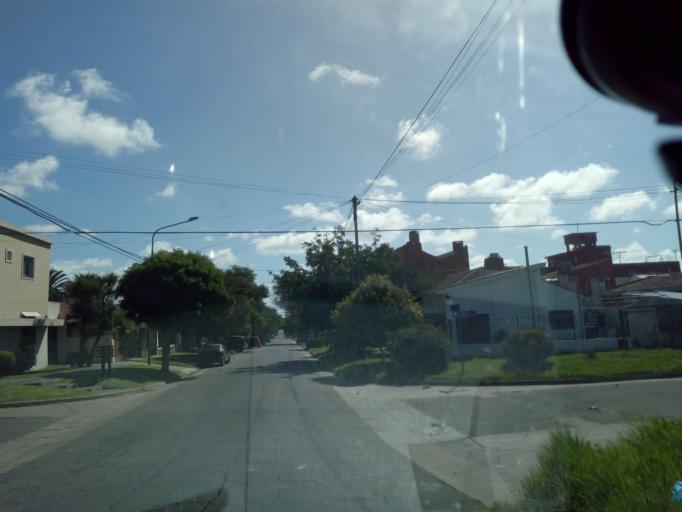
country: AR
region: Buenos Aires
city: Mar del Plata
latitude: -38.0550
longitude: -57.5528
